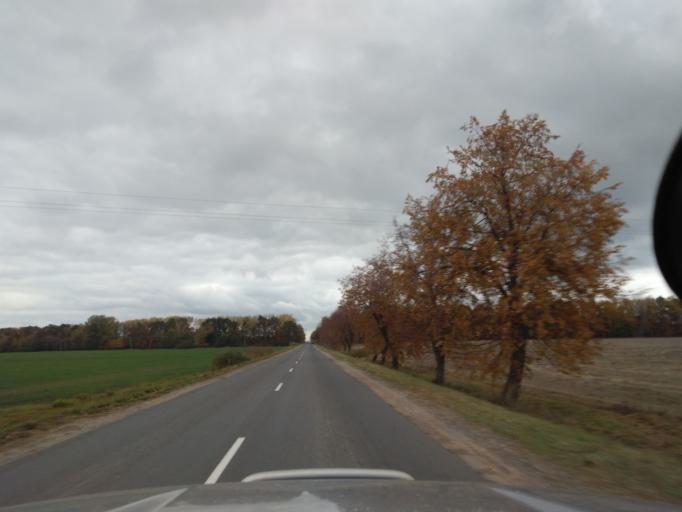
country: BY
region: Minsk
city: Slutsk
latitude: 53.2199
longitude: 27.3627
